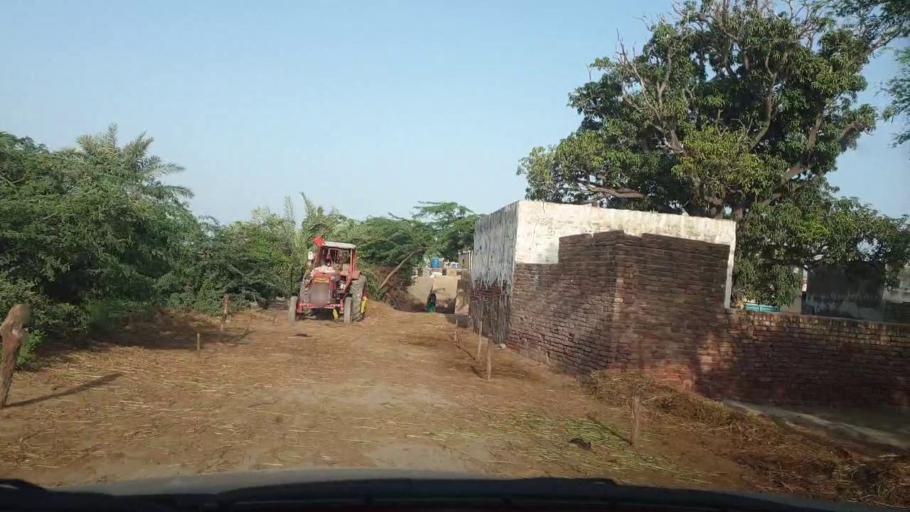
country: PK
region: Sindh
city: Talhar
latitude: 24.9108
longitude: 68.8148
